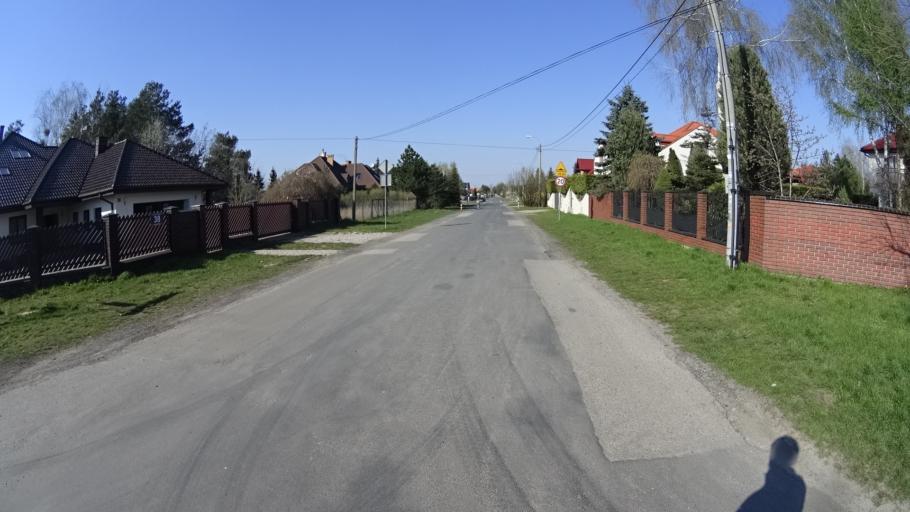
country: PL
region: Masovian Voivodeship
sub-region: Powiat warszawski zachodni
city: Babice
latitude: 52.2563
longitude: 20.8436
